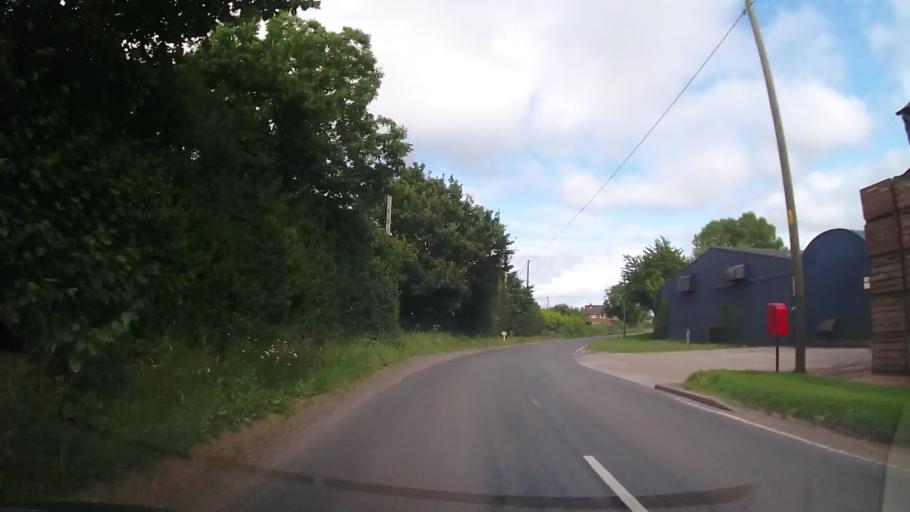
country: GB
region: England
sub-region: Shropshire
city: Great Ness
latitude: 52.7996
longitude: -2.9424
